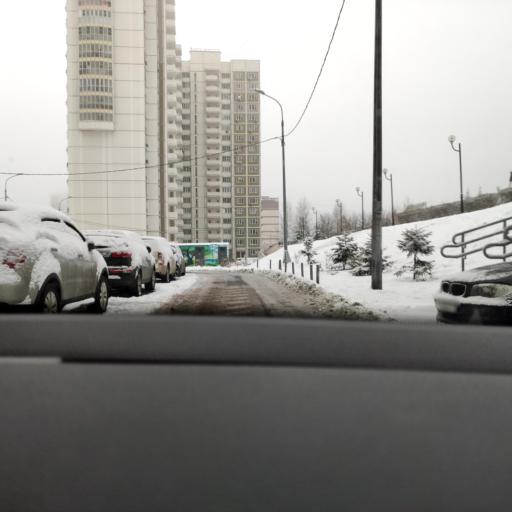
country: RU
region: Moscow
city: Chertanovo Yuzhnoye
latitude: 55.6128
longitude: 37.5787
